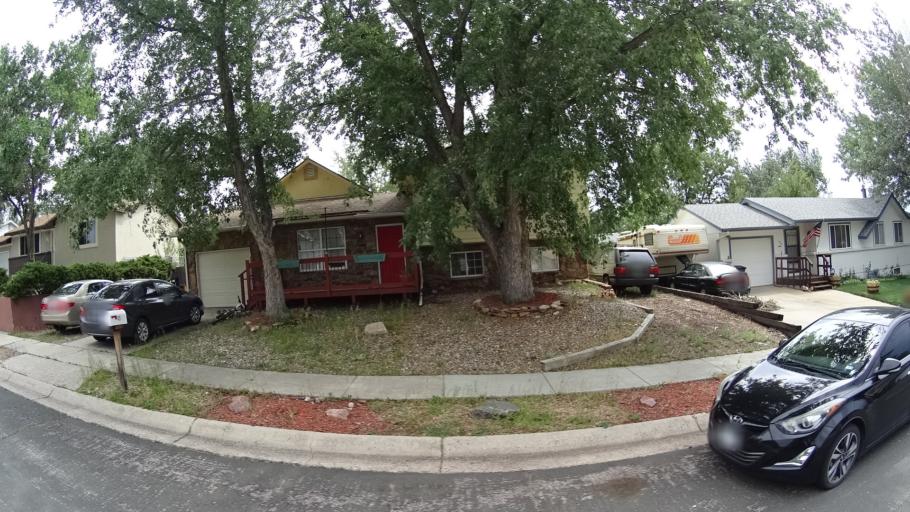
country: US
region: Colorado
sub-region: El Paso County
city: Colorado Springs
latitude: 38.8951
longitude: -104.8113
